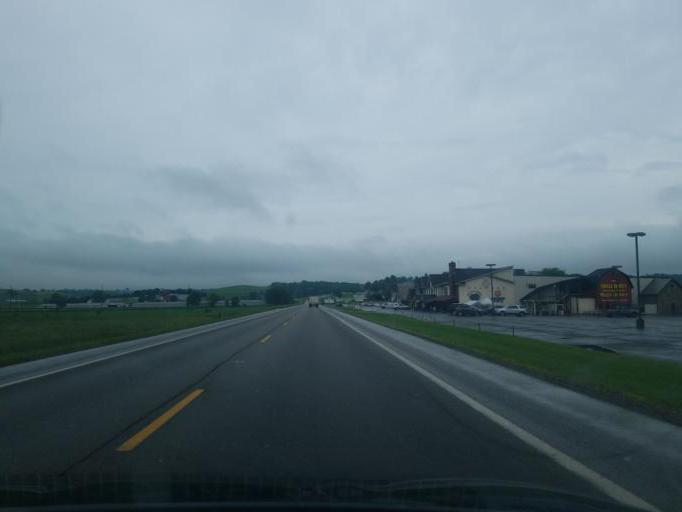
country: US
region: Ohio
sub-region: Tuscarawas County
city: Sugarcreek
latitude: 40.5270
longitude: -81.7167
